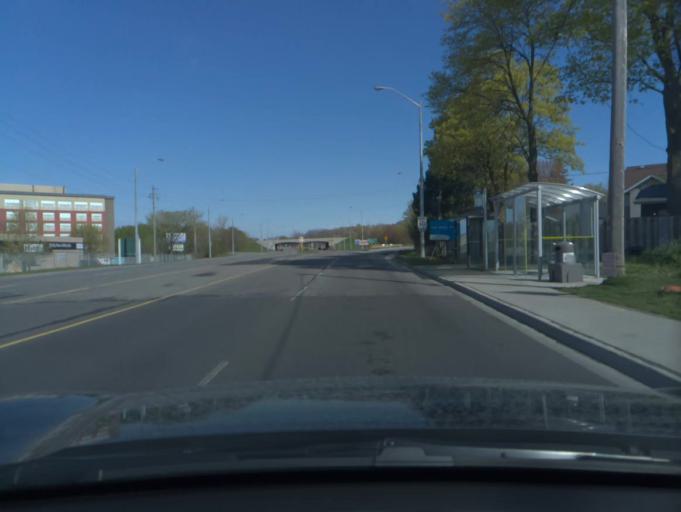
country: CA
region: Ontario
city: North Perth
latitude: 43.7995
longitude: -80.9998
